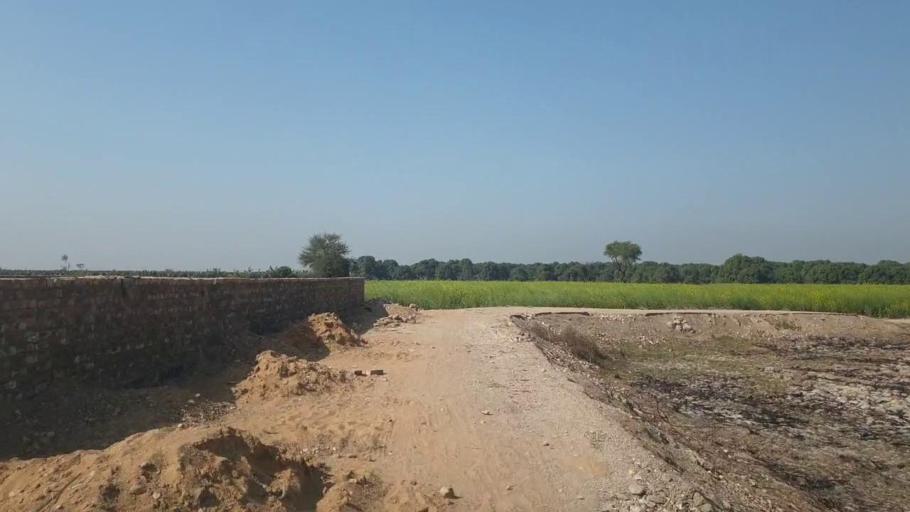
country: PK
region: Sindh
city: Tando Allahyar
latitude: 25.5686
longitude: 68.7390
